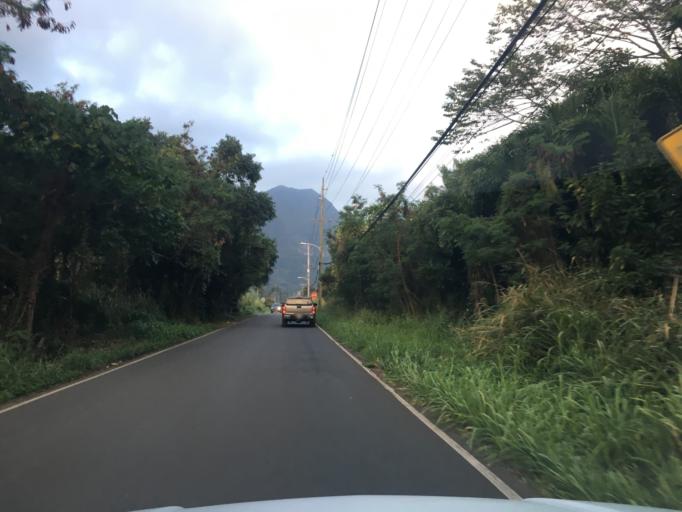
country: US
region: Hawaii
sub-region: Honolulu County
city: Waimanalo
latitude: 21.3422
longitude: -157.7293
